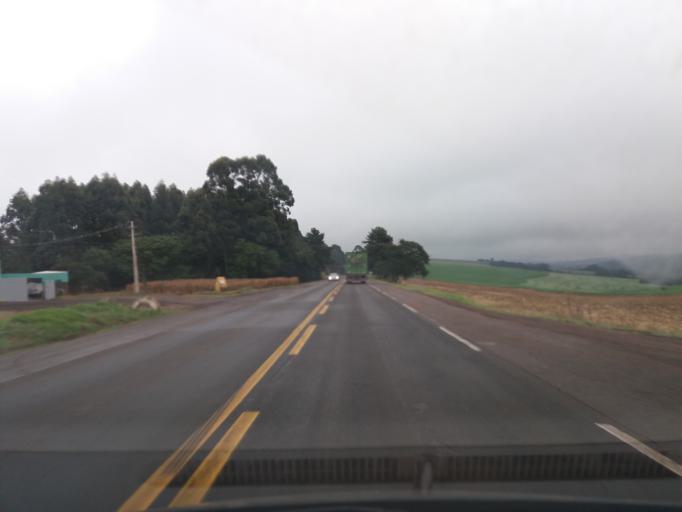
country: BR
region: Parana
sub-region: Ampere
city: Ampere
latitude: -25.9065
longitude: -53.4403
